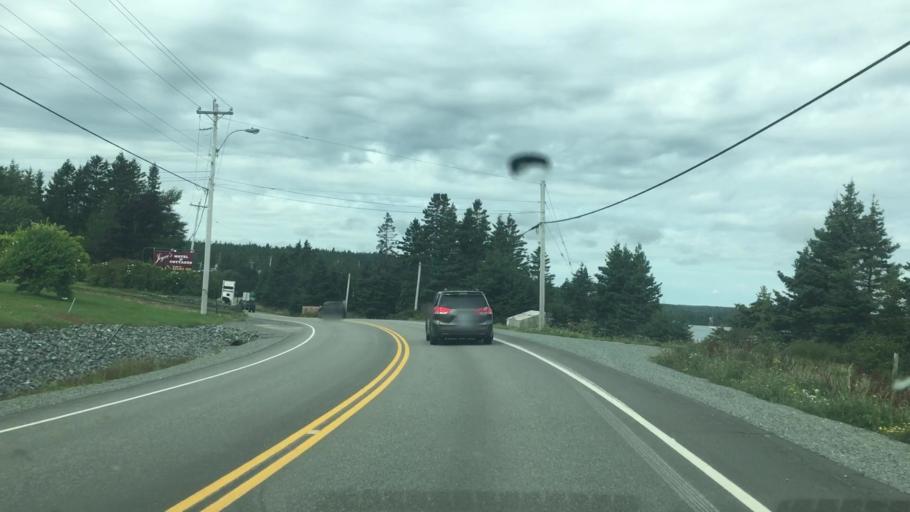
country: CA
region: Nova Scotia
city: Princeville
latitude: 45.6513
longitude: -60.8538
